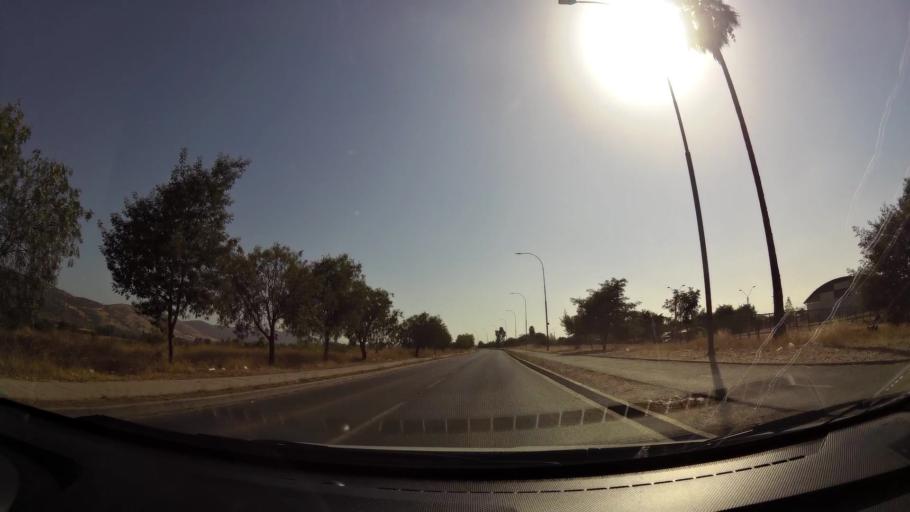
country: CL
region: Maule
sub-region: Provincia de Talca
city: Talca
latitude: -35.4017
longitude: -71.6603
